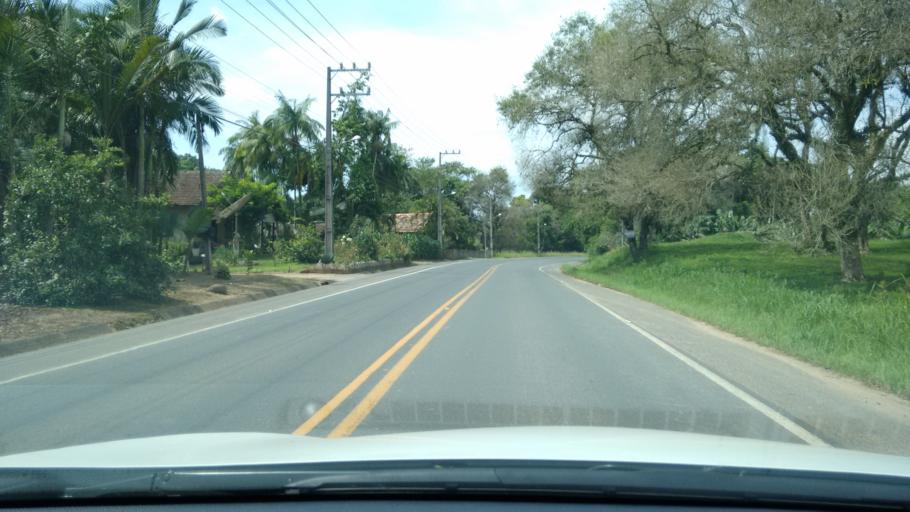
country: BR
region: Santa Catarina
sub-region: Timbo
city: Timbo
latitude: -26.8277
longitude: -49.3088
